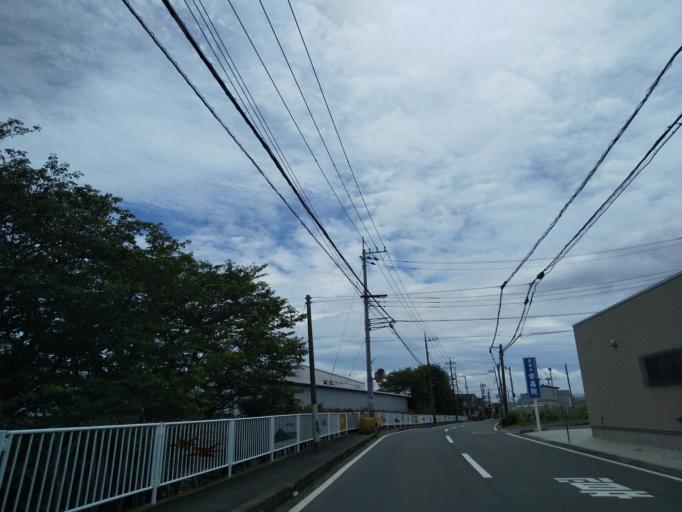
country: JP
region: Kanagawa
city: Zama
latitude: 35.4971
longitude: 139.3378
